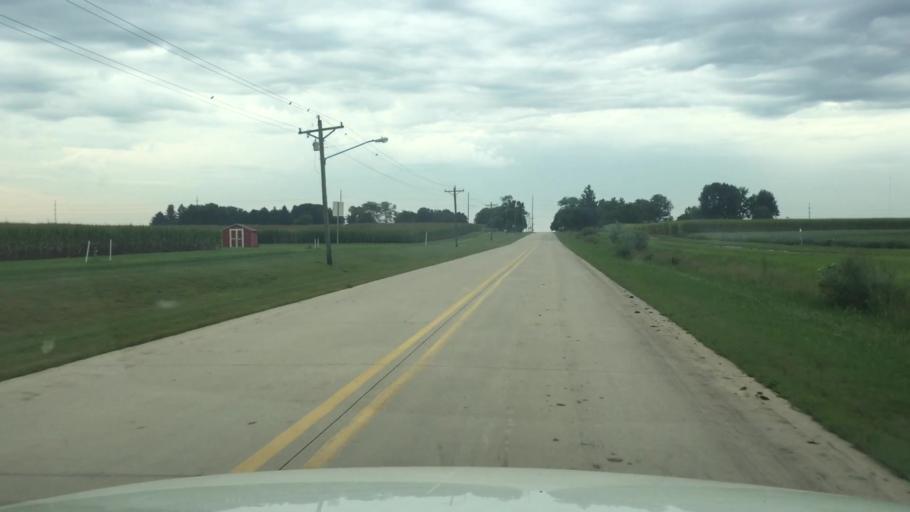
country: US
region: Iowa
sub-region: Story County
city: Huxley
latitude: 41.8829
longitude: -93.5809
